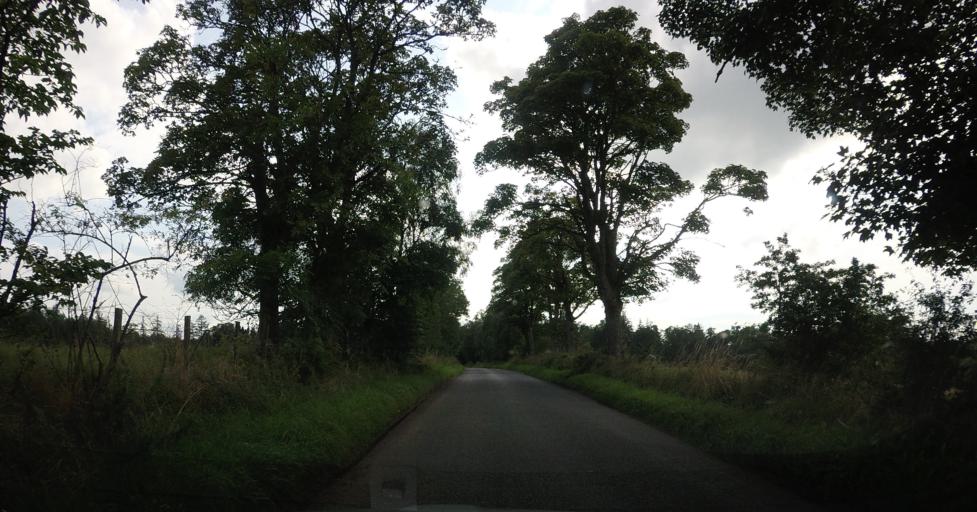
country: GB
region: Scotland
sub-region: Perth and Kinross
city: Auchterarder
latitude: 56.3099
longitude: -3.7350
